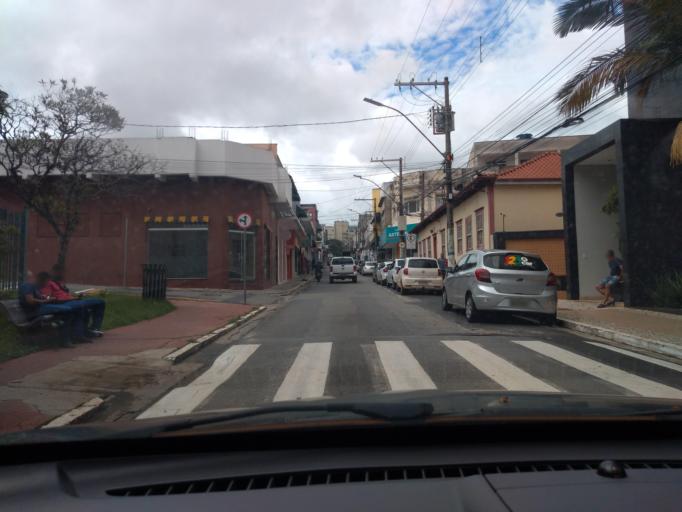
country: BR
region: Minas Gerais
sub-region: Lavras
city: Lavras
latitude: -21.2376
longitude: -44.9983
